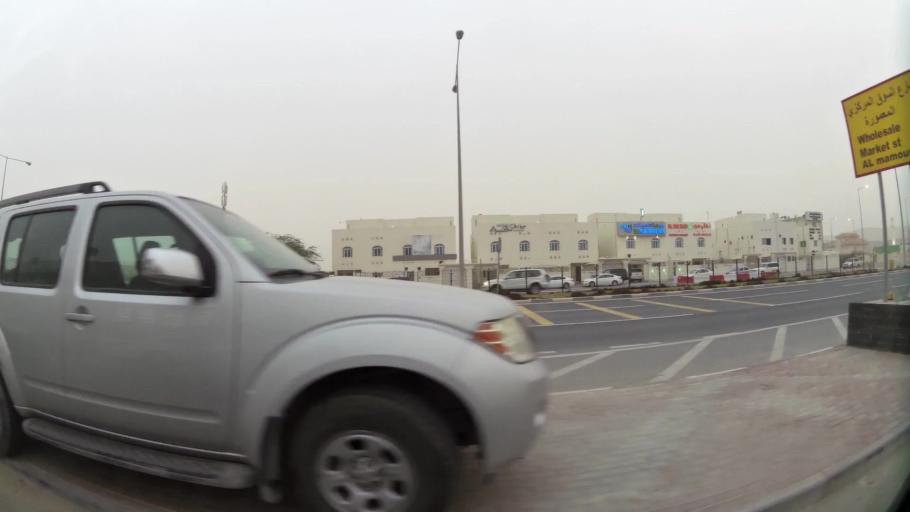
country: QA
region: Baladiyat ad Dawhah
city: Doha
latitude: 25.2343
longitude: 51.5014
